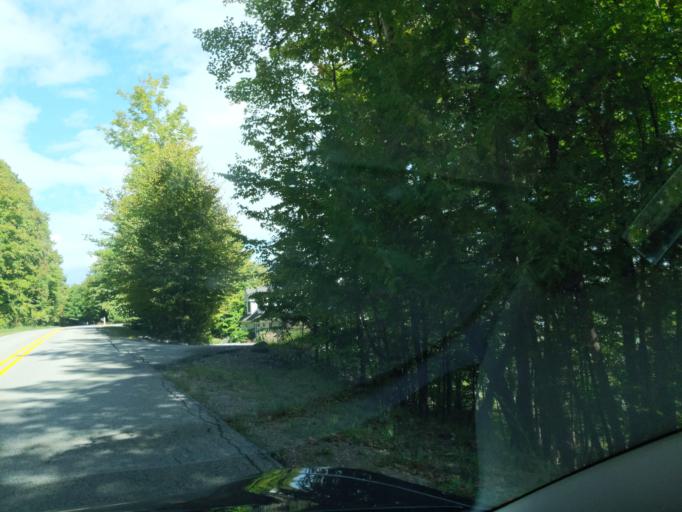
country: US
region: Michigan
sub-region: Antrim County
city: Bellaire
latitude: 44.9636
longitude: -85.3231
